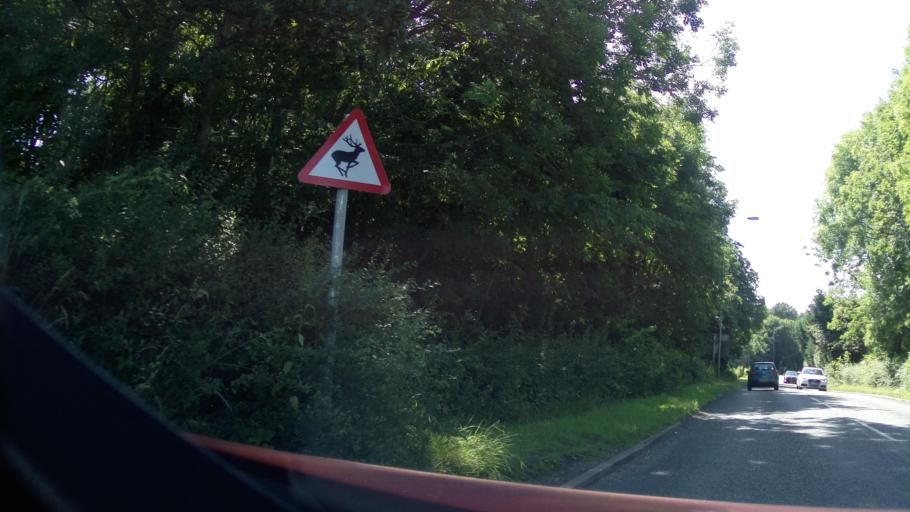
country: GB
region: England
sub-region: Warwickshire
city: Studley
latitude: 52.2987
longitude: -1.8845
